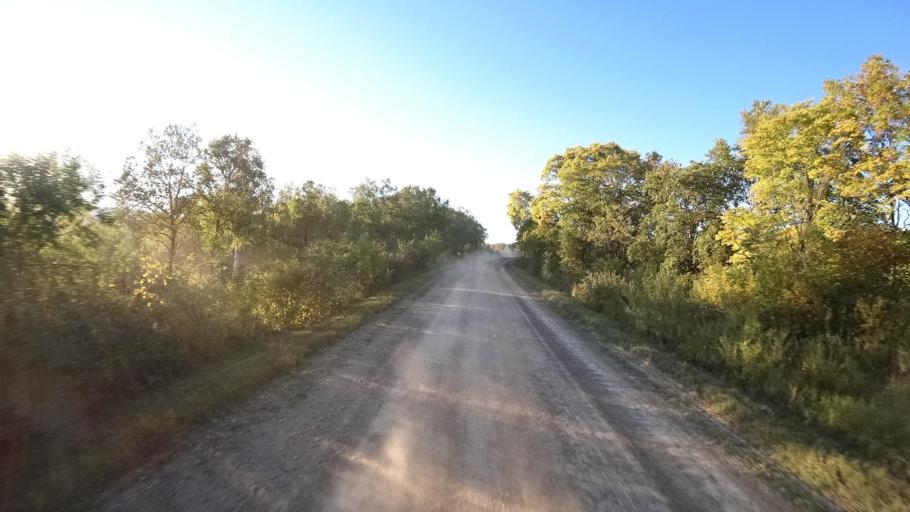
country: RU
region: Primorskiy
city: Kirovskiy
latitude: 44.8177
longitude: 133.6098
